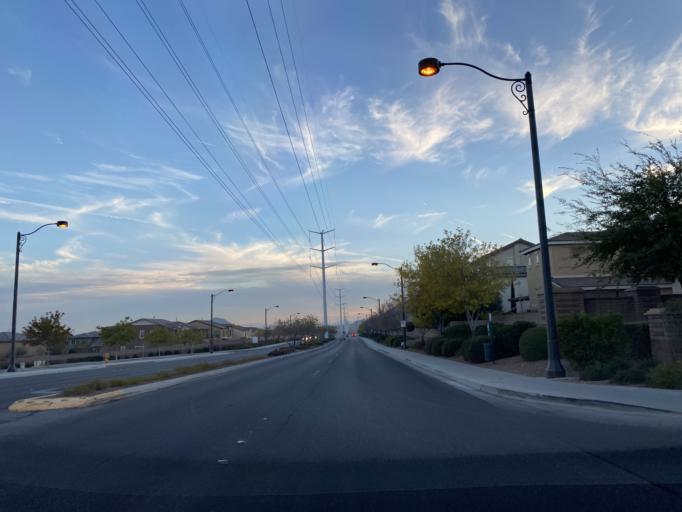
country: US
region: Nevada
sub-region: Clark County
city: Summerlin South
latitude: 36.2817
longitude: -115.3289
